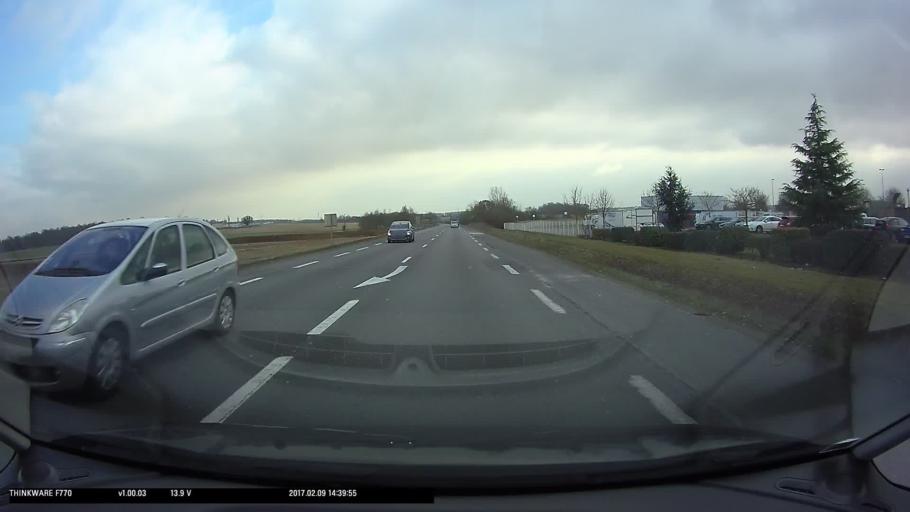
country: FR
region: Centre
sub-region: Departement du Cher
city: La Chapelle-Saint-Ursin
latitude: 47.0440
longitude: 2.3474
